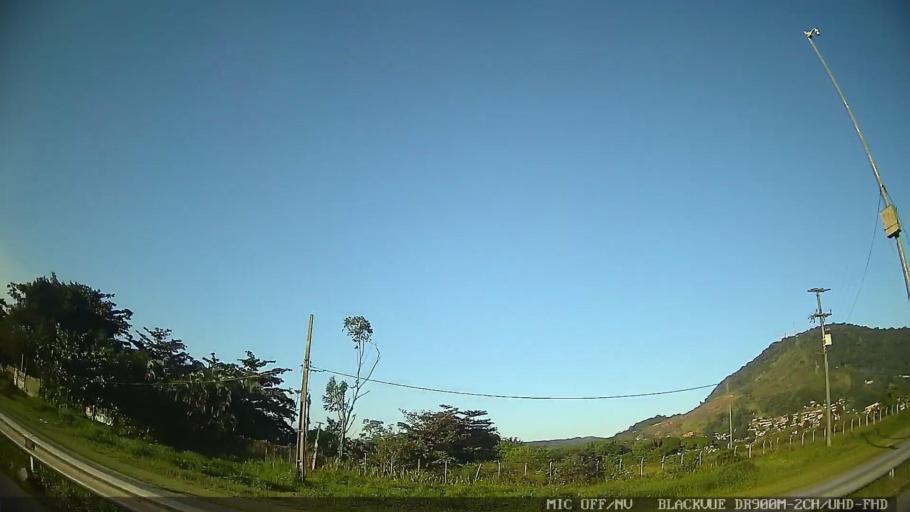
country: BR
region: Sao Paulo
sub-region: Guaruja
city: Guaruja
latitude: -23.9760
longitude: -46.2685
